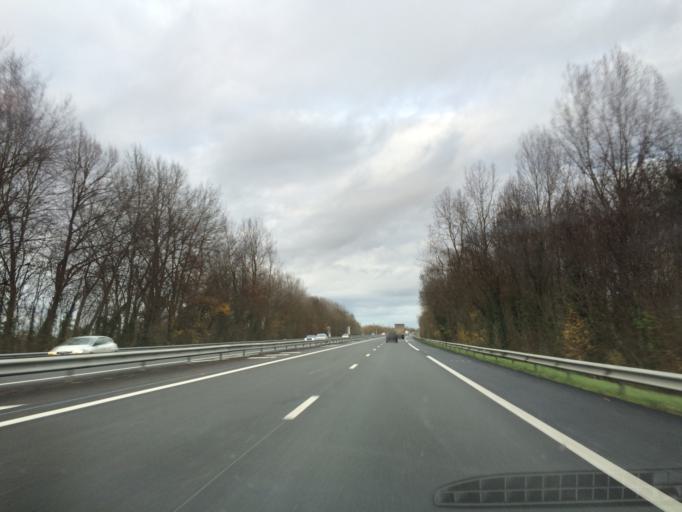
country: FR
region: Poitou-Charentes
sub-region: Departement des Deux-Sevres
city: Fors
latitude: 46.2550
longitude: -0.4219
